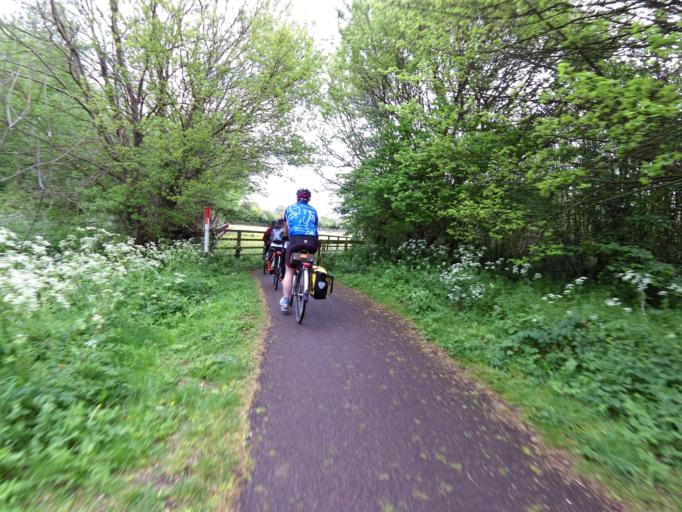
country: GB
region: England
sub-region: Cambridgeshire
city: Cambridge
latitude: 52.2179
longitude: 0.1664
